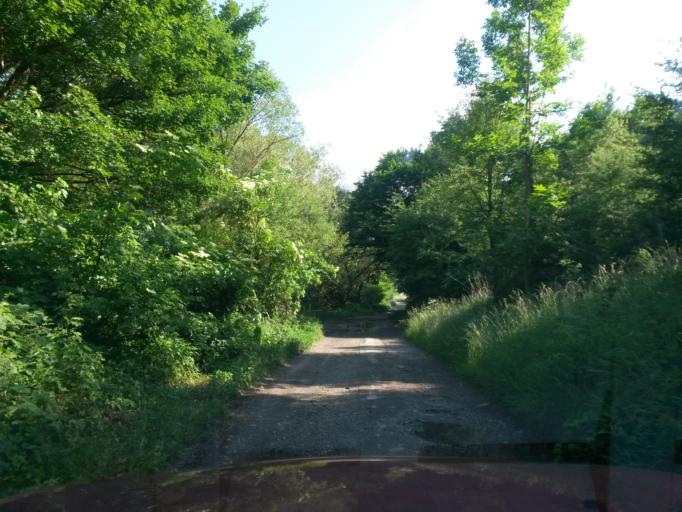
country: SK
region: Kosicky
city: Roznava
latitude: 48.5901
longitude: 20.6441
